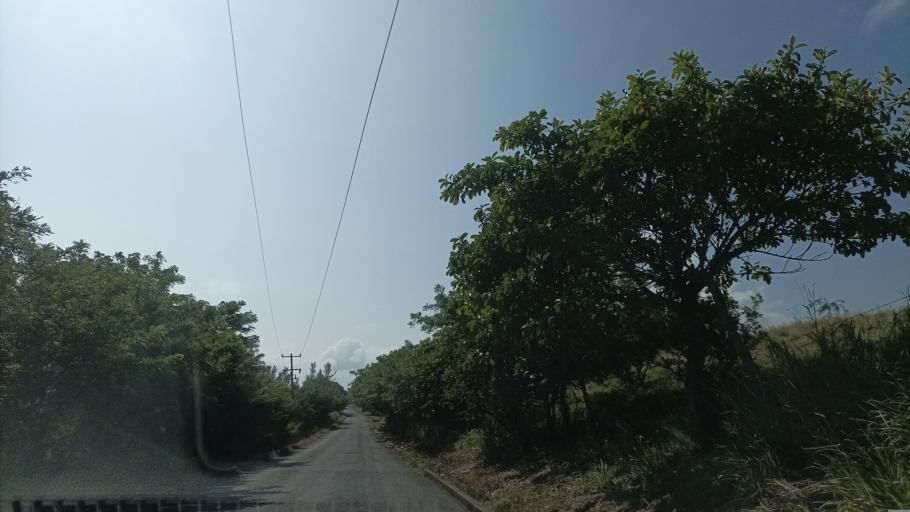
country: MX
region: Veracruz
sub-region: Pajapan
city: Pajapan
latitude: 18.2231
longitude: -94.6167
